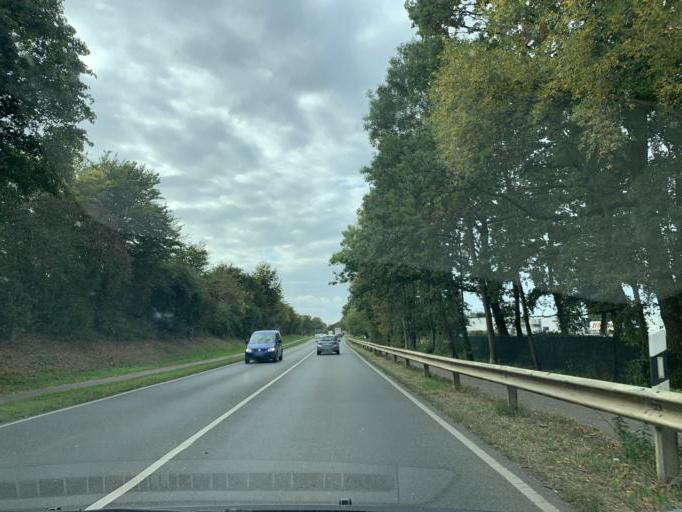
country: DE
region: North Rhine-Westphalia
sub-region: Regierungsbezirk Koln
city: Wassenberg
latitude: 51.0897
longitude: 6.1603
